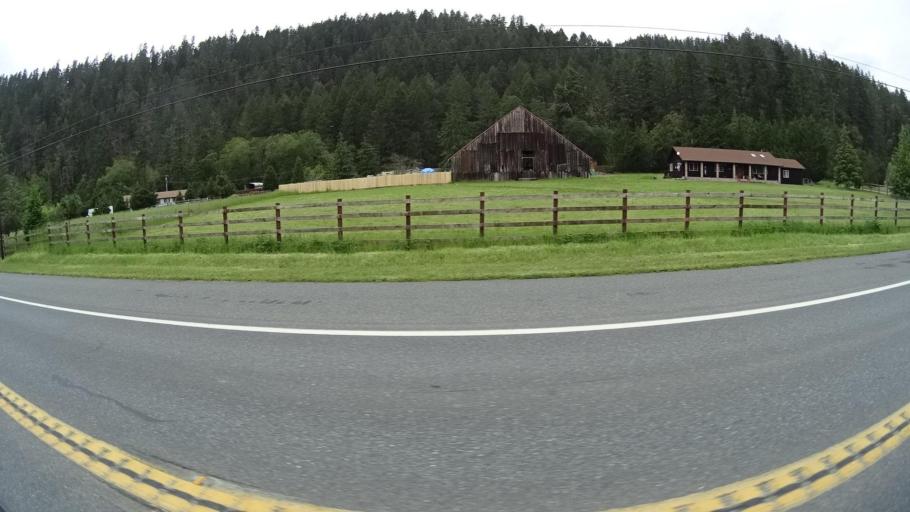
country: US
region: California
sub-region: Humboldt County
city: Willow Creek
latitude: 40.9574
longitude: -123.6430
